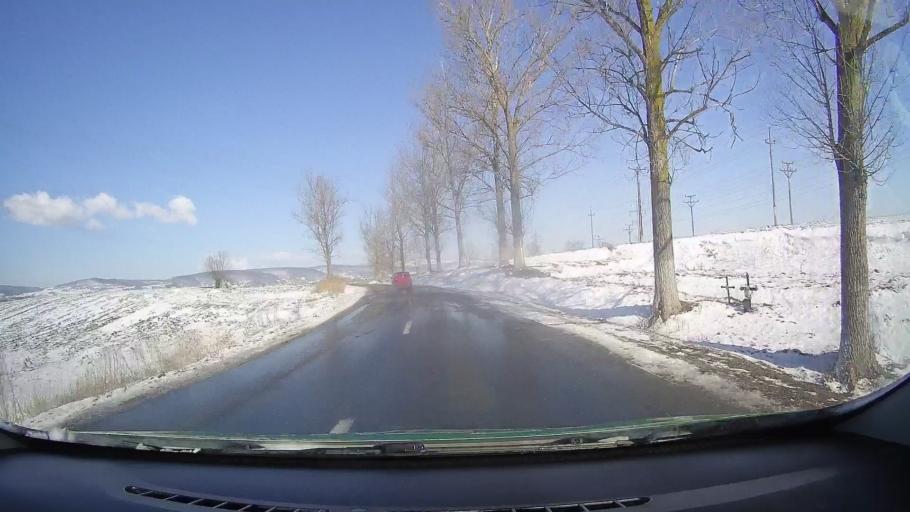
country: RO
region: Sibiu
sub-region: Comuna Avrig
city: Marsa
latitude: 45.7085
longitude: 24.3694
